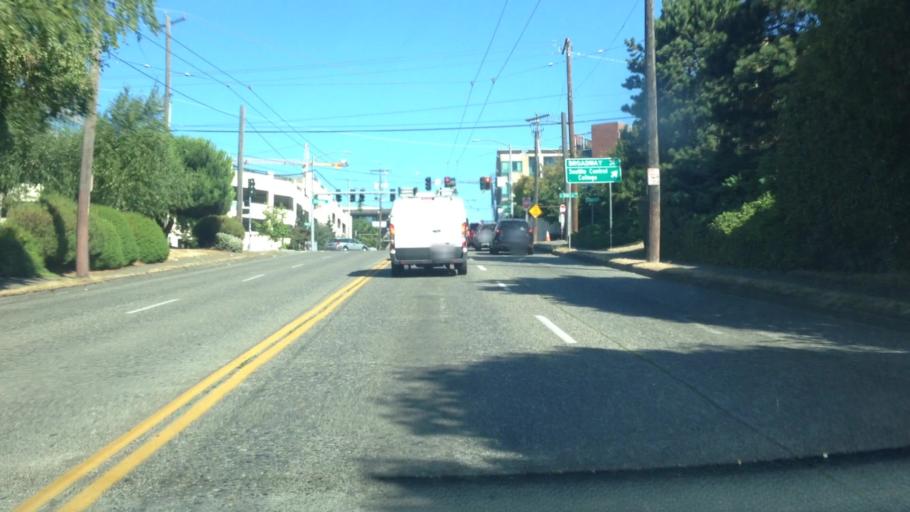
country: US
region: Washington
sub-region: King County
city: Seattle
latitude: 47.6039
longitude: -122.3200
